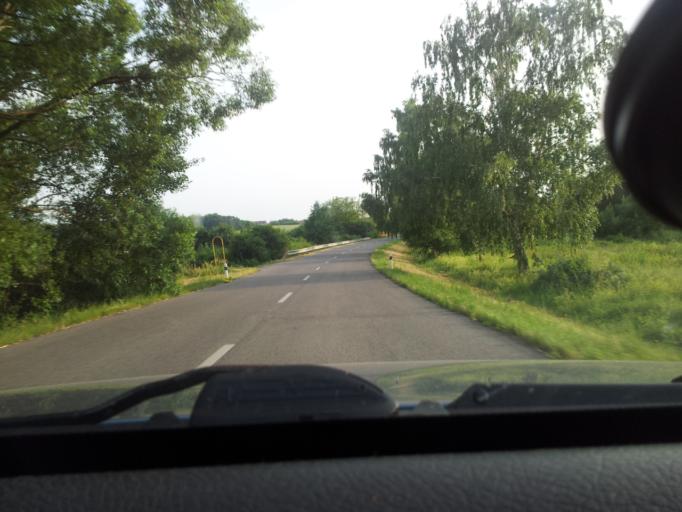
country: SK
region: Banskobystricky
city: Nova Bana
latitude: 48.3343
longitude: 18.7197
